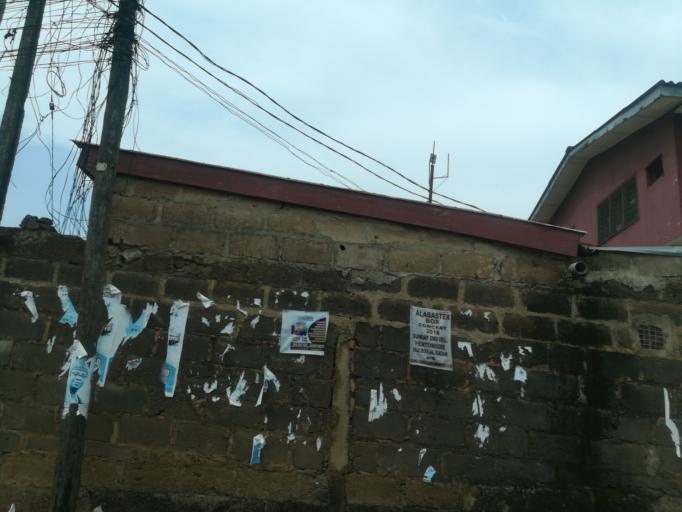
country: NG
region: Oyo
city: Ibadan
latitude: 7.4242
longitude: 3.9180
